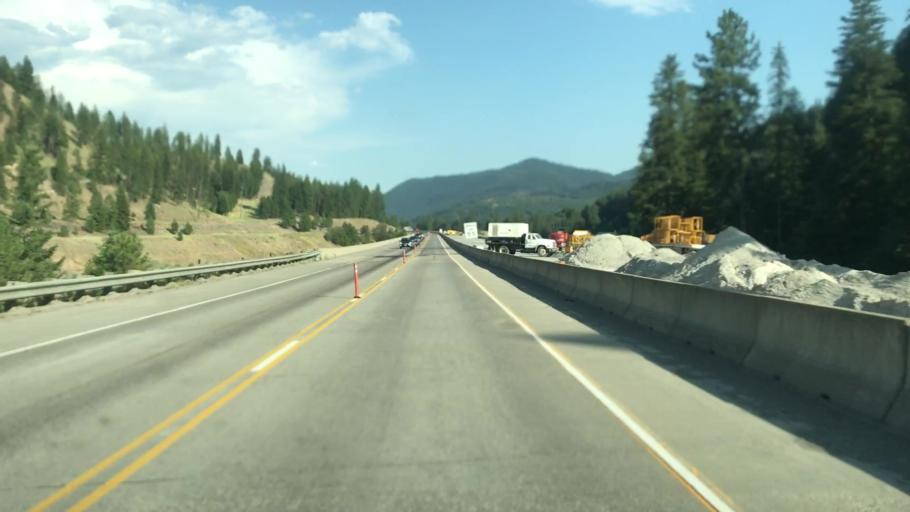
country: US
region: Montana
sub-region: Mineral County
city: Superior
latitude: 47.2222
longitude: -114.9634
